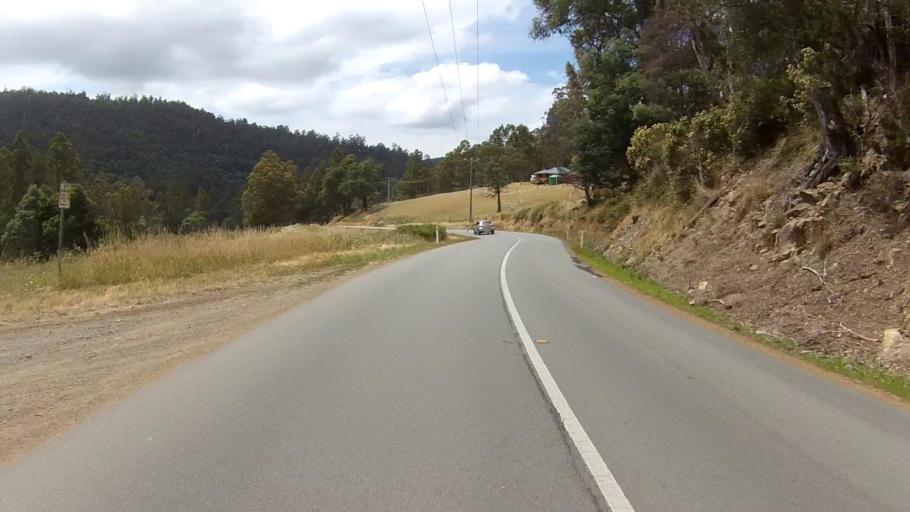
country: AU
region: Tasmania
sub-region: Kingborough
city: Kettering
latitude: -43.1055
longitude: 147.2055
